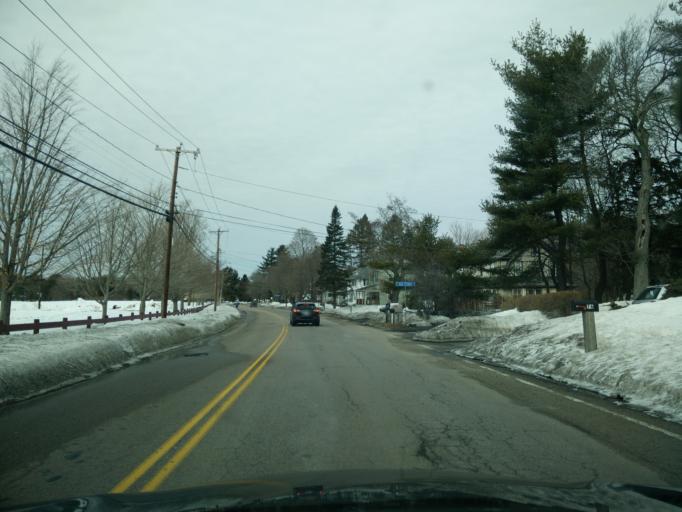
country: US
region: Massachusetts
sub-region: Norfolk County
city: Walpole
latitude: 42.1653
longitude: -71.2370
